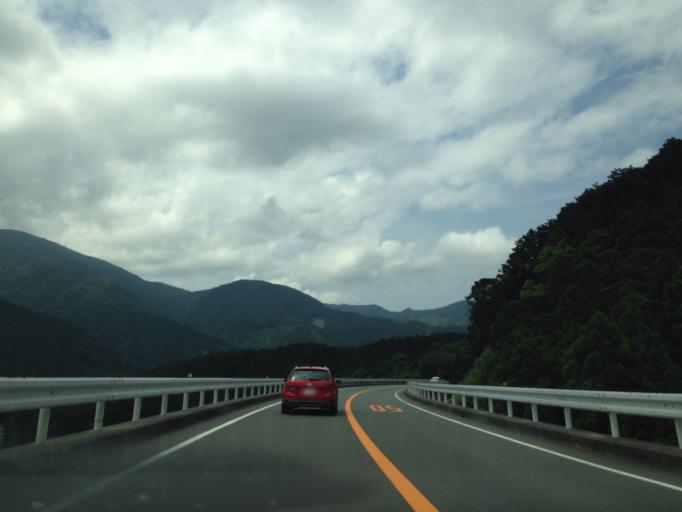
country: JP
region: Shizuoka
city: Heda
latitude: 34.9167
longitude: 138.8249
